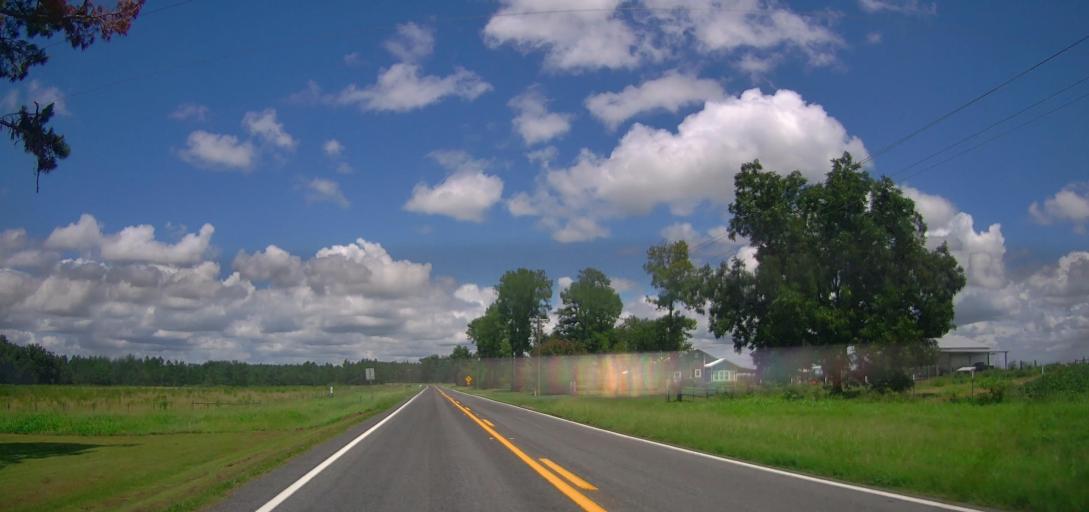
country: US
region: Georgia
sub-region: Turner County
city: Ashburn
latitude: 31.7429
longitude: -83.6473
